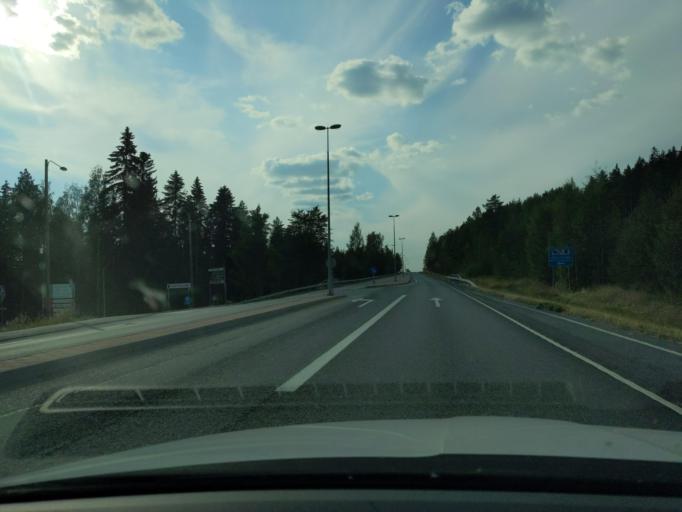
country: FI
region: Paijanne Tavastia
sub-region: Lahti
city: Asikkala
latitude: 61.1626
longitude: 25.5750
